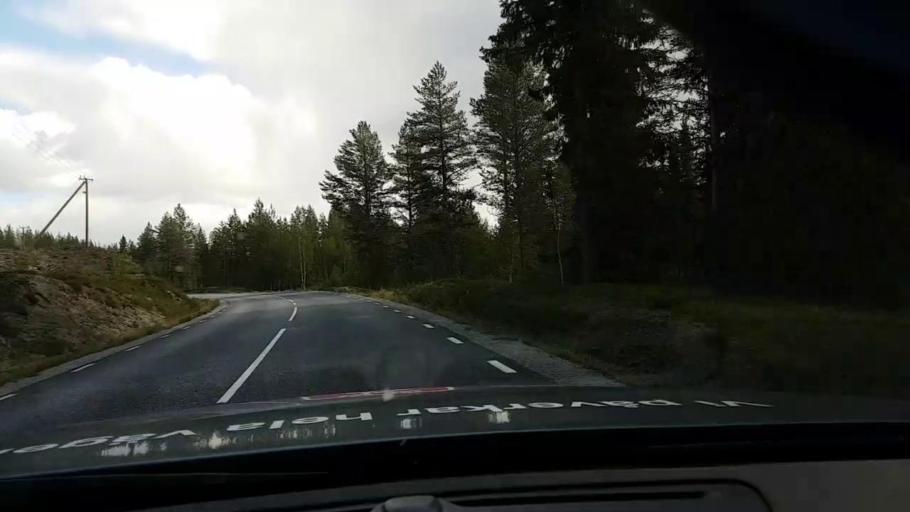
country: SE
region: Vaesterbotten
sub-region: Asele Kommun
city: Asele
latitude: 63.8498
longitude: 17.3979
